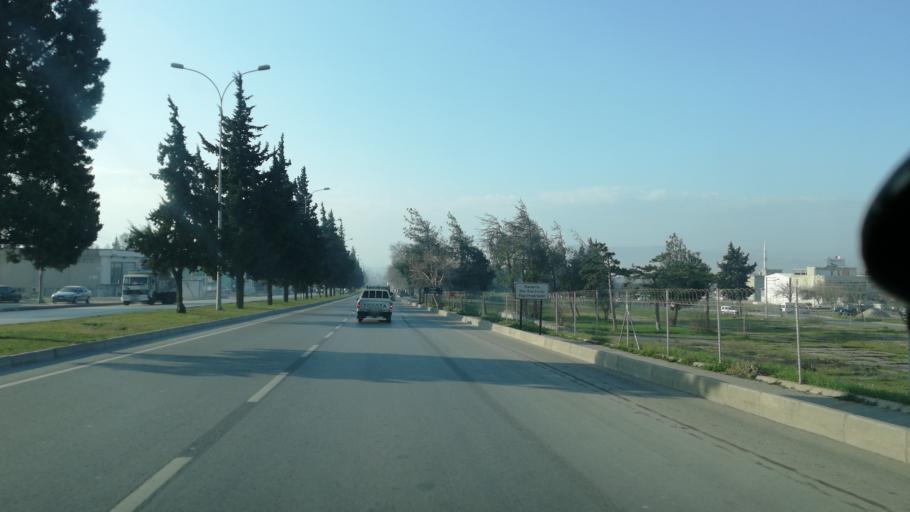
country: TR
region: Kahramanmaras
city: Kahramanmaras
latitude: 37.5651
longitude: 36.9241
